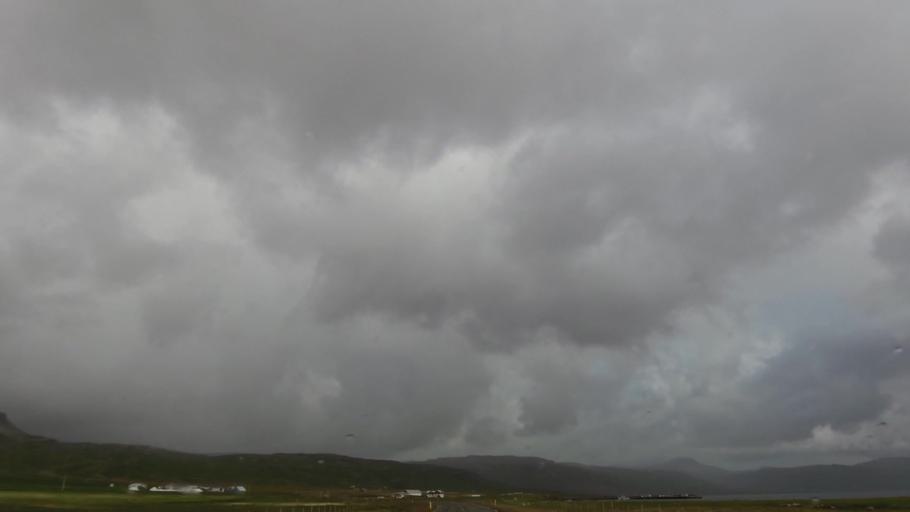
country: IS
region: Westfjords
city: Isafjoerdur
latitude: 65.5222
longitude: -23.1879
